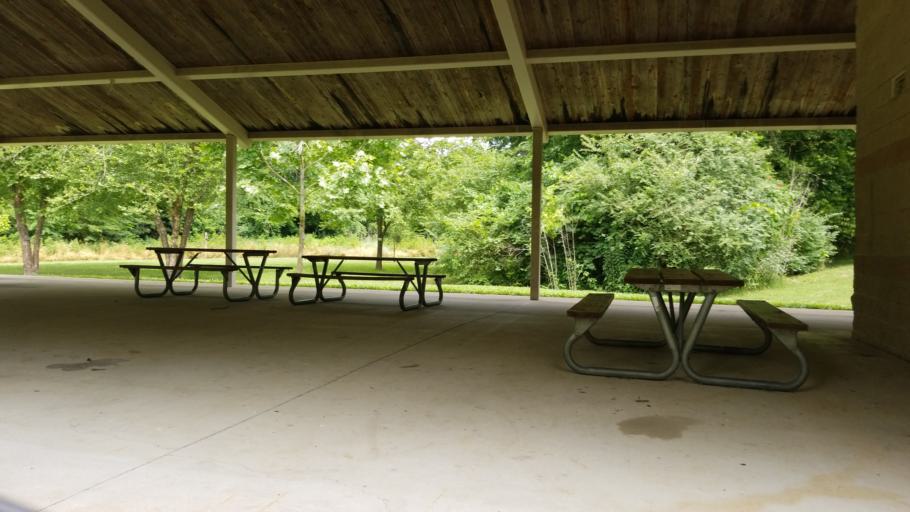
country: US
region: Tennessee
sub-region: Davidson County
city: Forest Hills
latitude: 36.0360
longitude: -86.8396
